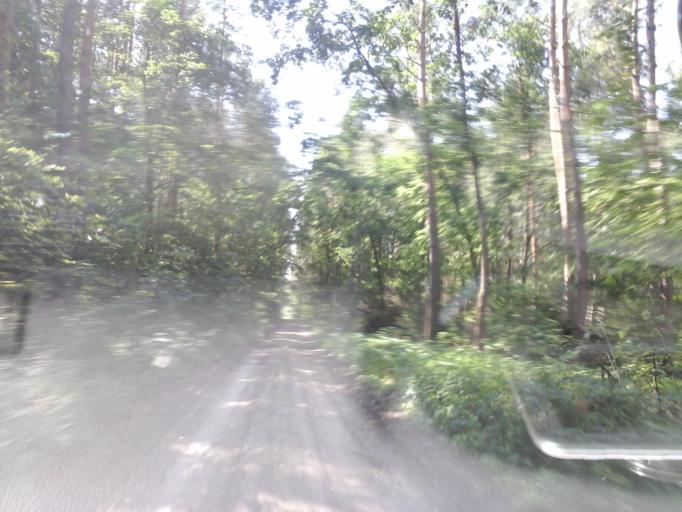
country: PL
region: West Pomeranian Voivodeship
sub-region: Powiat choszczenski
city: Bierzwnik
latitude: 53.0166
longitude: 15.6791
